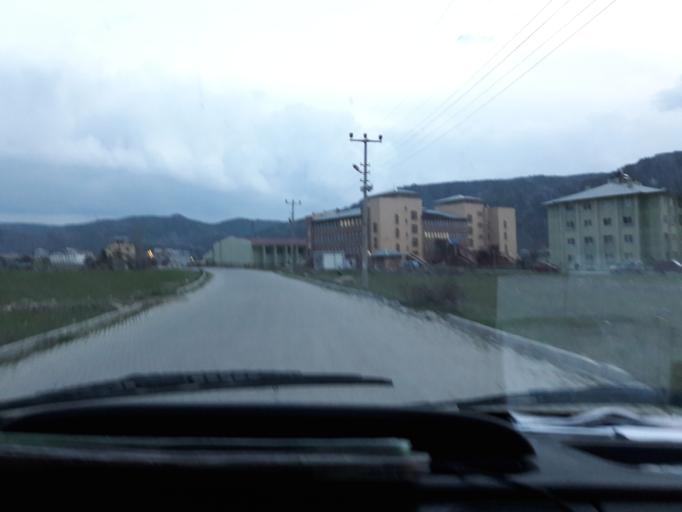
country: TR
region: Giresun
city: Alucra
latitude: 40.3249
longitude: 38.7711
